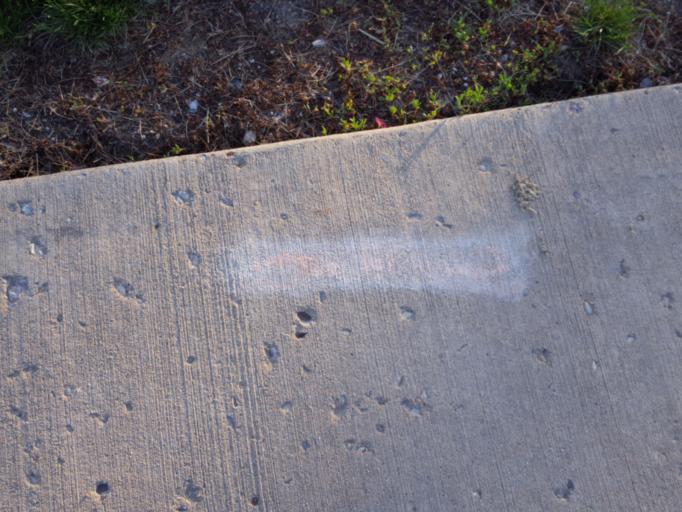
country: US
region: Illinois
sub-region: Lake County
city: Deerfield
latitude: 42.1524
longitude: -87.8354
